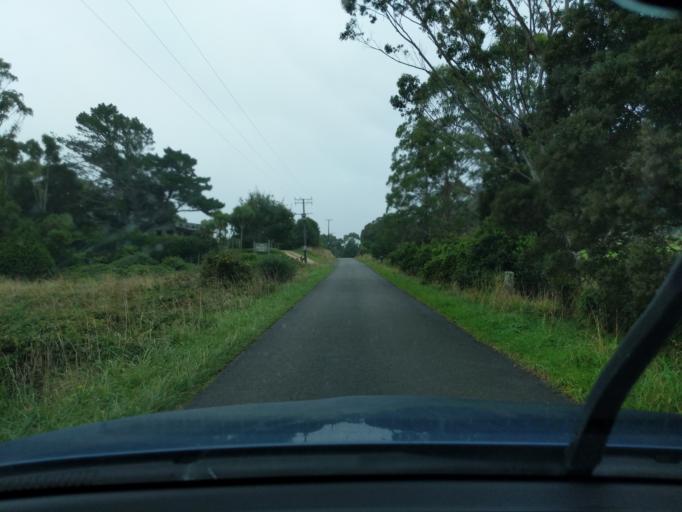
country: NZ
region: Tasman
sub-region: Tasman District
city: Takaka
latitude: -40.6381
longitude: 172.4877
